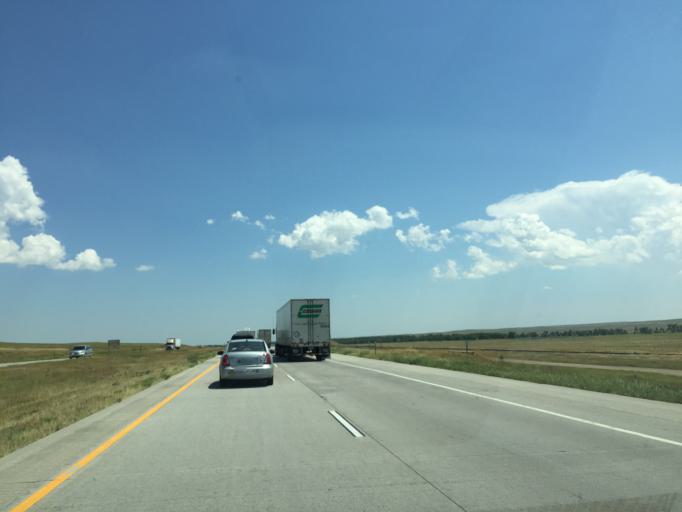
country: US
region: Colorado
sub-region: Lincoln County
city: Limon
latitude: 39.2914
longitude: -103.7957
